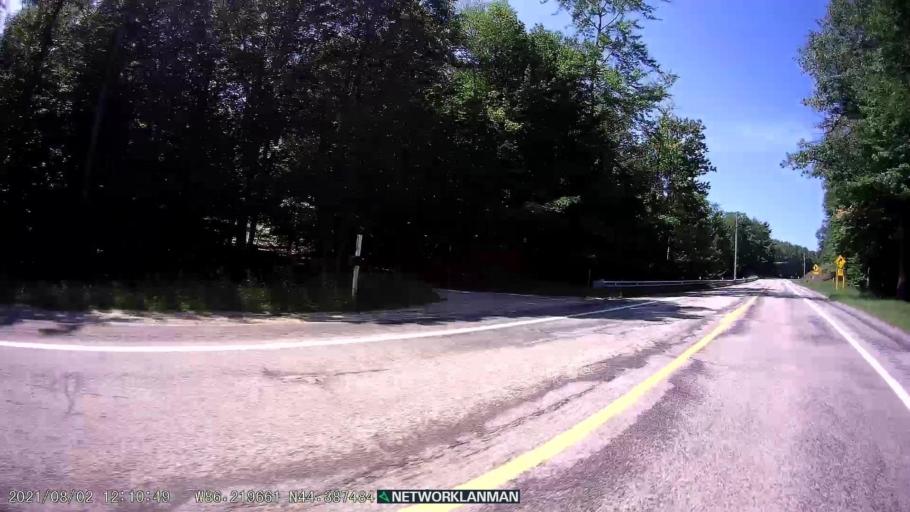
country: US
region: Michigan
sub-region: Manistee County
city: Manistee
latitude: 44.3877
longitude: -86.2198
